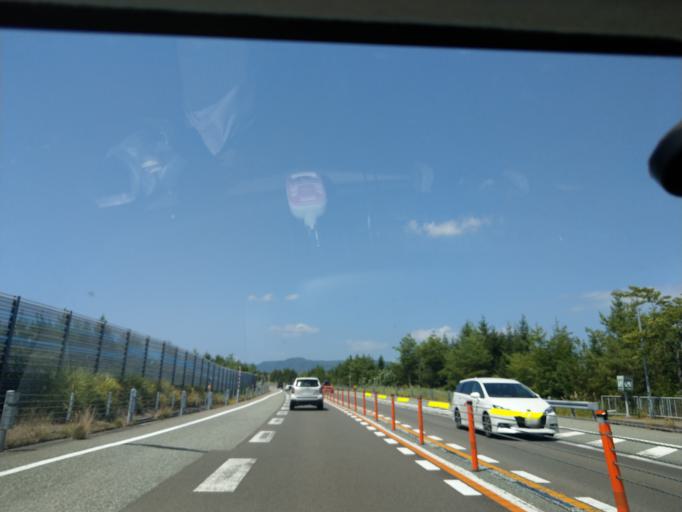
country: JP
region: Akita
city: Omagari
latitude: 39.3976
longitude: 140.4754
